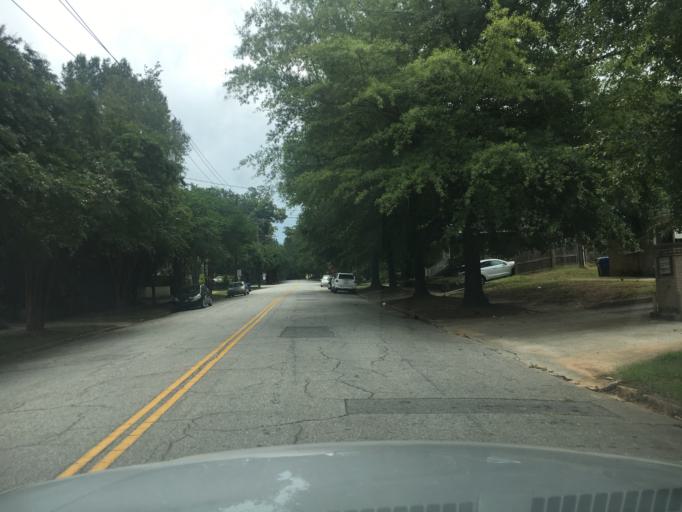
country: US
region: South Carolina
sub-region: Greenville County
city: Greenville
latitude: 34.8577
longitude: -82.4086
